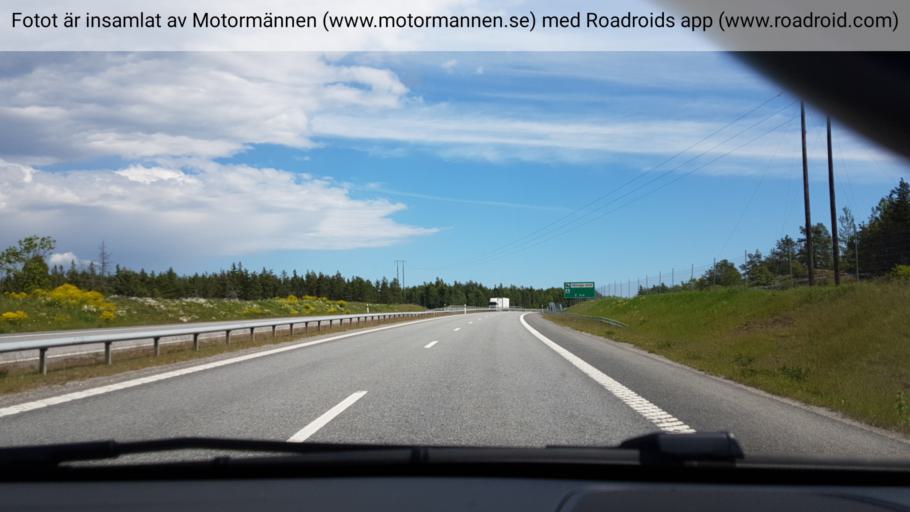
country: SE
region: Stockholm
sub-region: Nynashamns Kommun
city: Osmo
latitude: 59.0589
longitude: 18.0123
